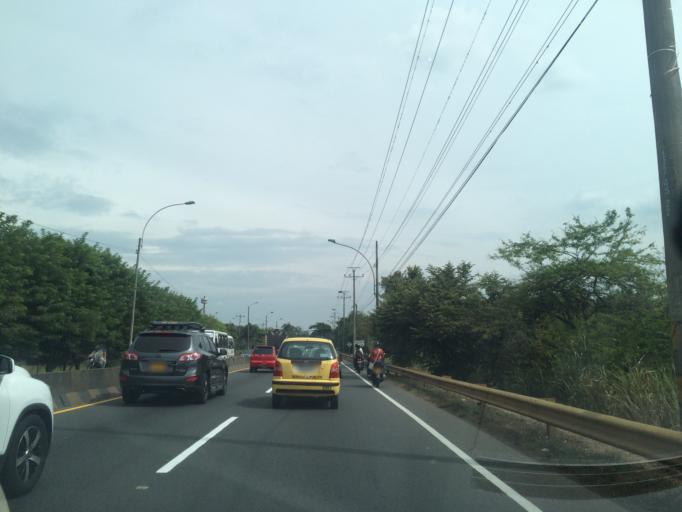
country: CO
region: Valle del Cauca
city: Cali
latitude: 3.3501
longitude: -76.5237
